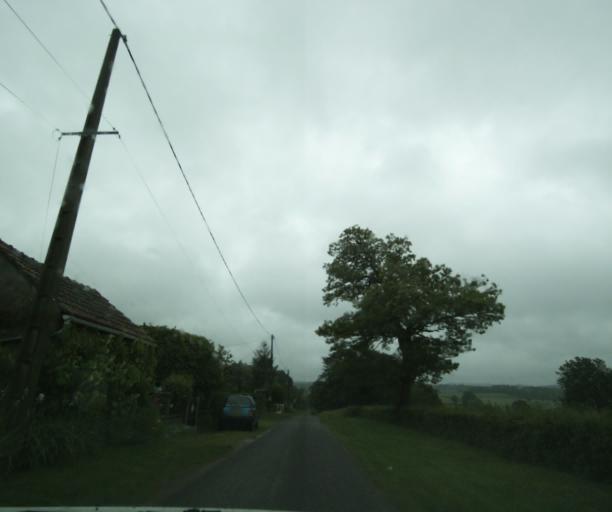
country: FR
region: Bourgogne
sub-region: Departement de Saone-et-Loire
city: Genelard
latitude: 46.5597
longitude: 4.2458
